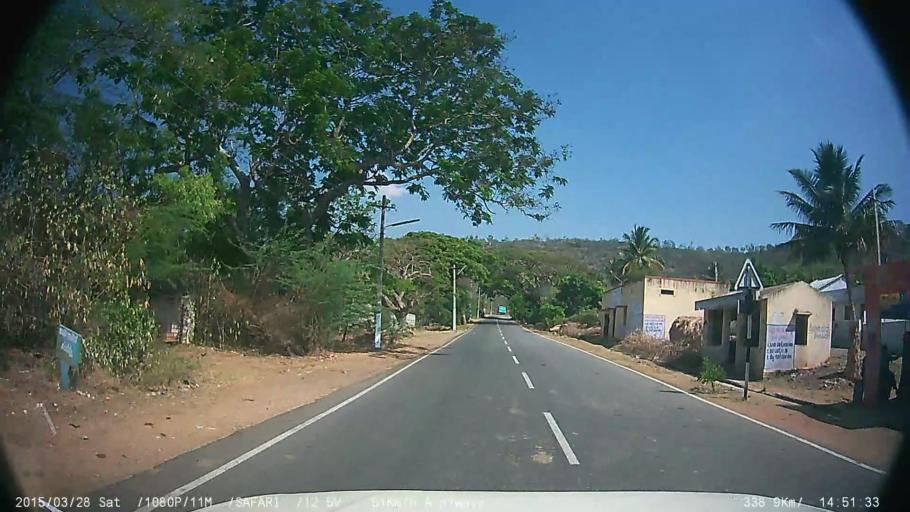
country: IN
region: Karnataka
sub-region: Mysore
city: Mysore
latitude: 12.2885
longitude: 76.6852
